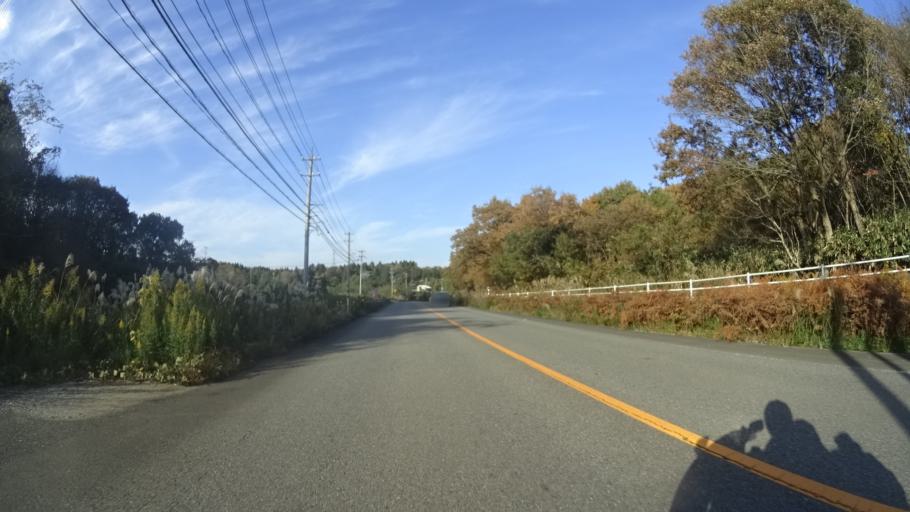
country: JP
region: Ishikawa
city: Hakui
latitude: 37.0541
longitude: 136.7764
